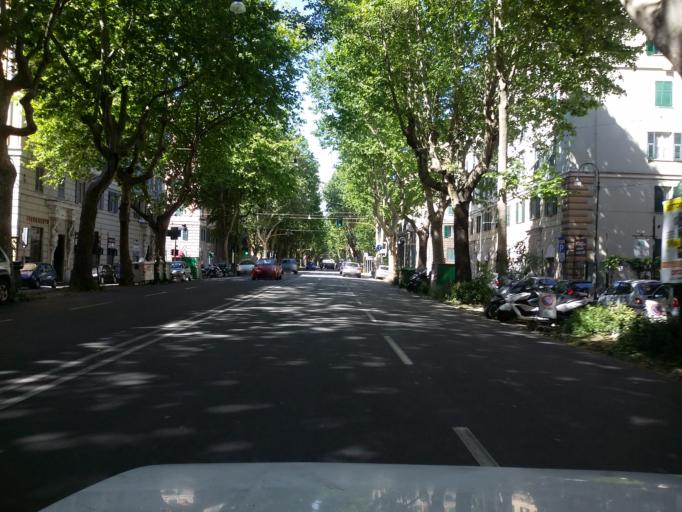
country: IT
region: Liguria
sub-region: Provincia di Genova
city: San Teodoro
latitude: 44.3990
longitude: 8.9493
